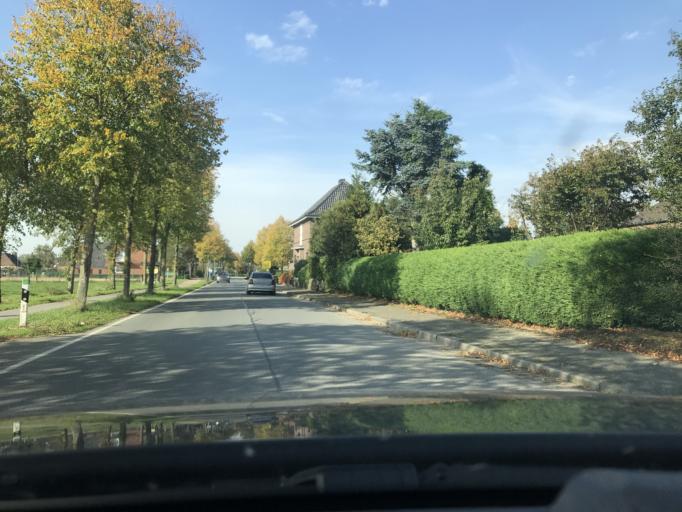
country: DE
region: North Rhine-Westphalia
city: Kalkar
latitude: 51.7618
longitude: 6.2594
